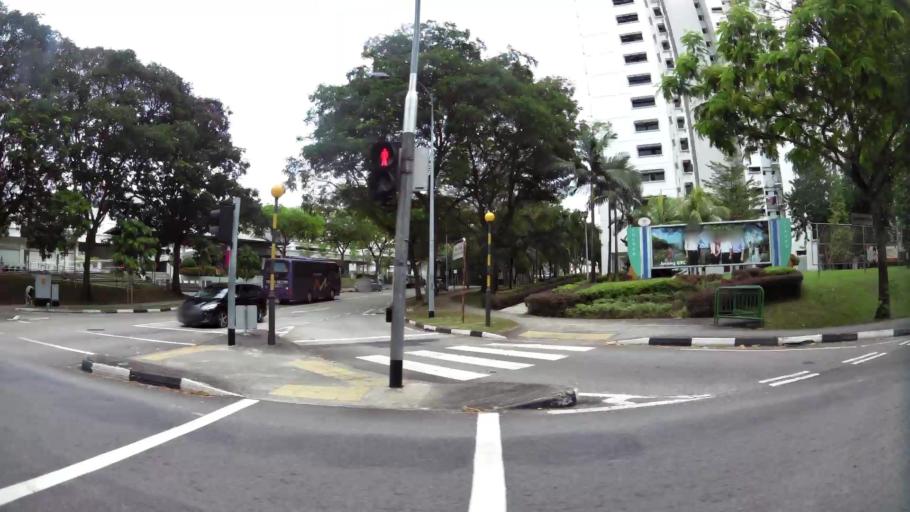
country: MY
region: Johor
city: Johor Bahru
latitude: 1.3338
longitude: 103.7202
